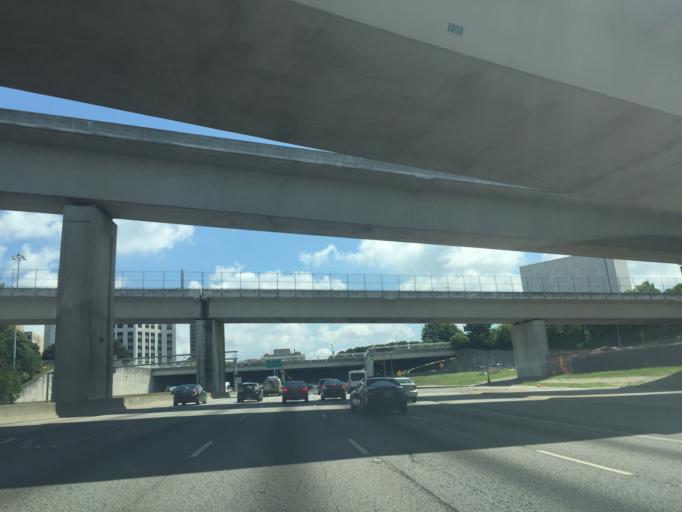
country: US
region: Georgia
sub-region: Fulton County
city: Atlanta
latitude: 33.7448
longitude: -84.3901
